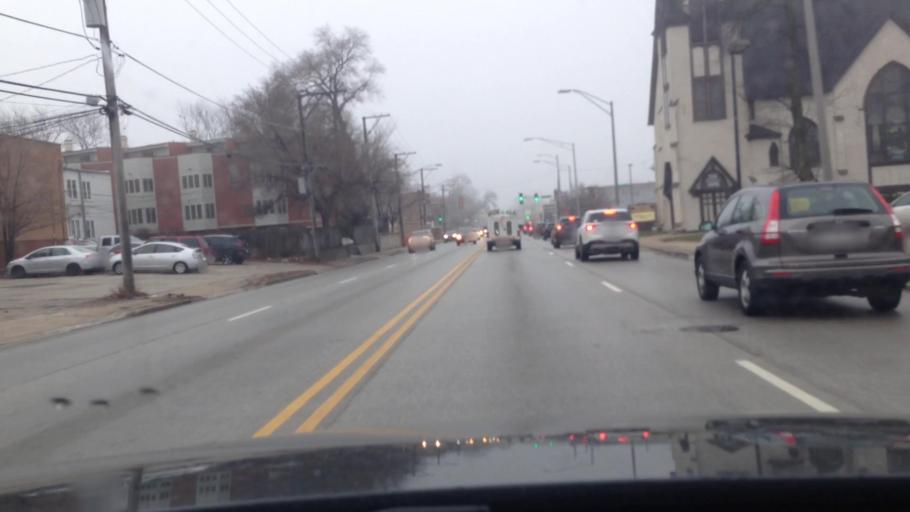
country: US
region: Illinois
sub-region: Cook County
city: Forest Park
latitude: 41.8847
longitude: -87.8049
